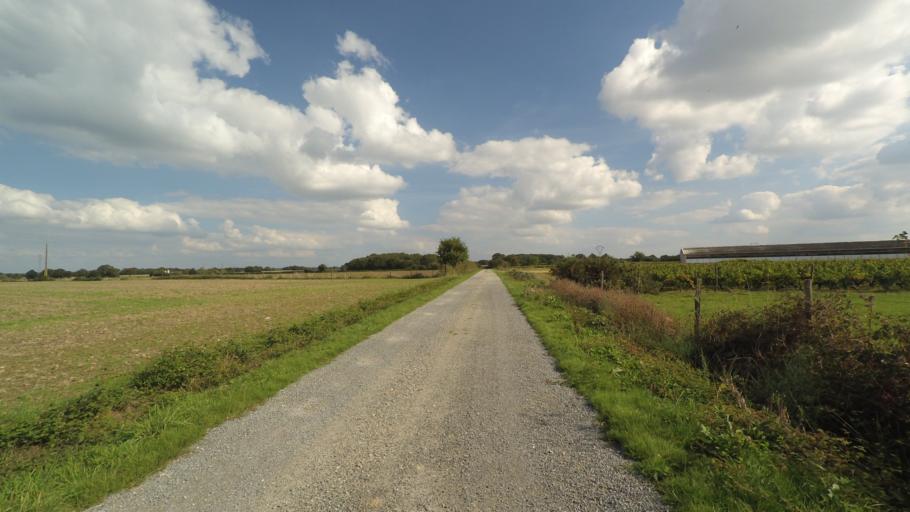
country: FR
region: Pays de la Loire
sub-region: Departement de la Loire-Atlantique
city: Vieillevigne
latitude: 46.9773
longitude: -1.4080
